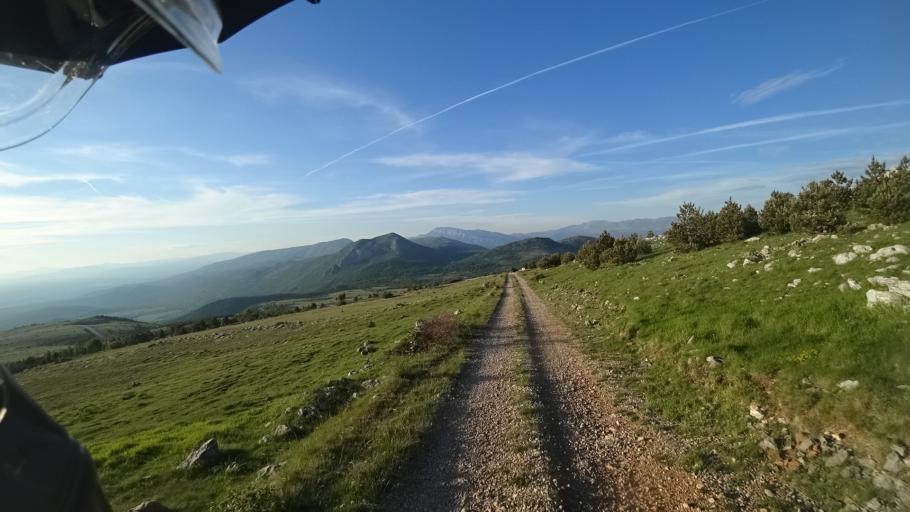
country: HR
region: Sibensko-Kniniska
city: Drnis
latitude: 43.8836
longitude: 16.3402
